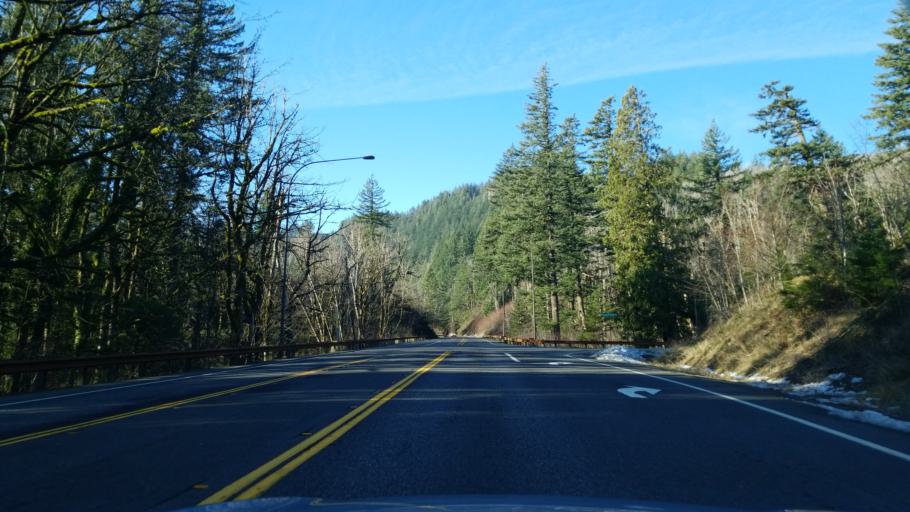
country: US
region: Washington
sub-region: Clark County
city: Washougal
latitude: 45.5888
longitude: -122.1779
